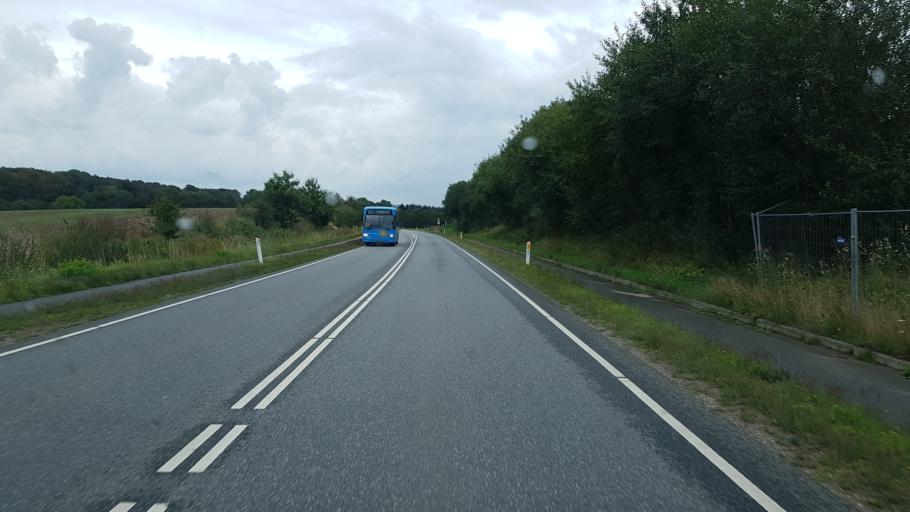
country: DK
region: Central Jutland
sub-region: Horsens Kommune
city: Braedstrup
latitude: 55.9090
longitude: 9.7217
